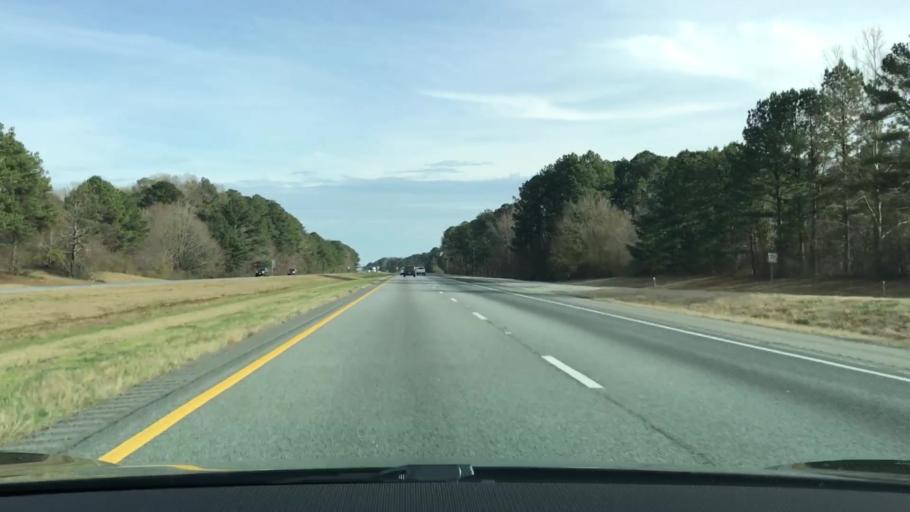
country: US
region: Georgia
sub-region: Walton County
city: Social Circle
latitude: 33.5920
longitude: -83.6276
